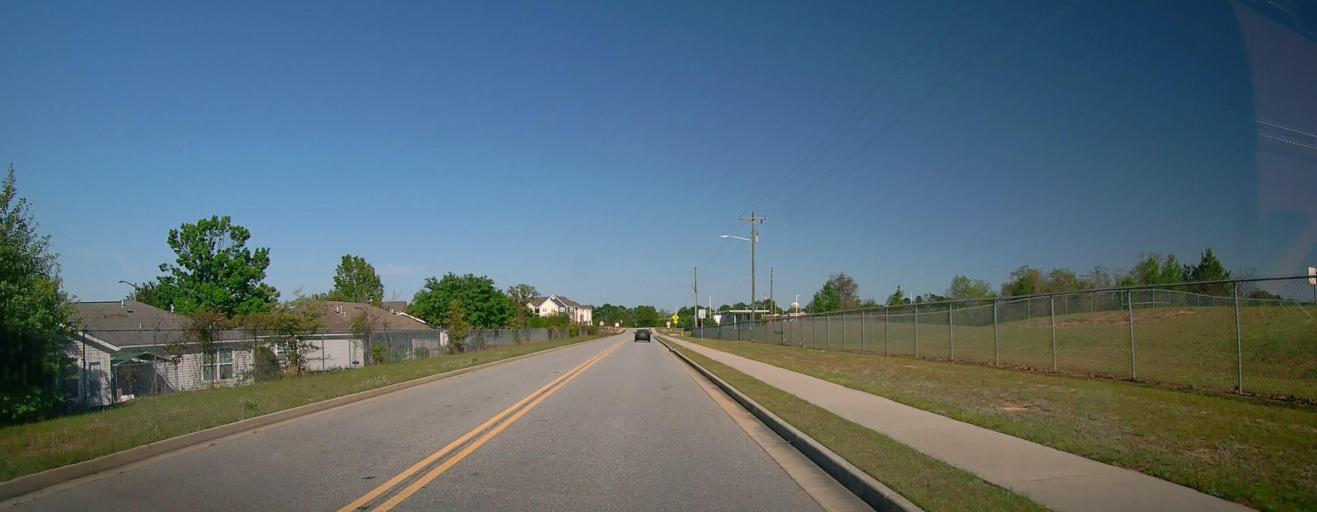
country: US
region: Georgia
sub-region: Houston County
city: Robins Air Force Base
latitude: 32.6017
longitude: -83.6000
